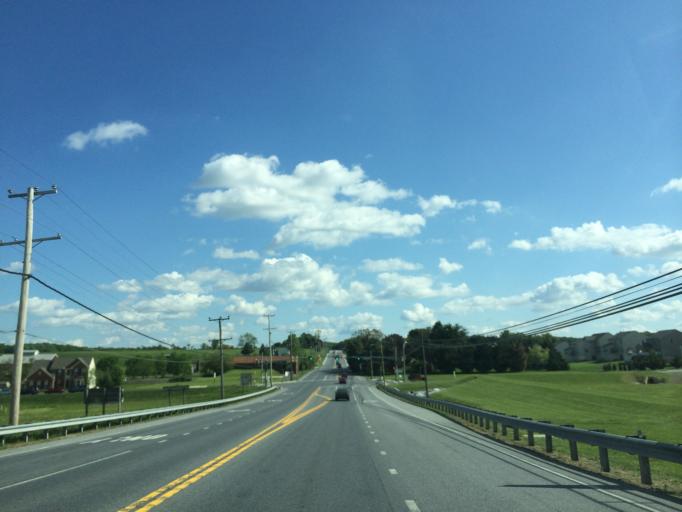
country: US
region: Maryland
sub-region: Carroll County
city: Manchester
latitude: 39.6799
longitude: -76.8918
